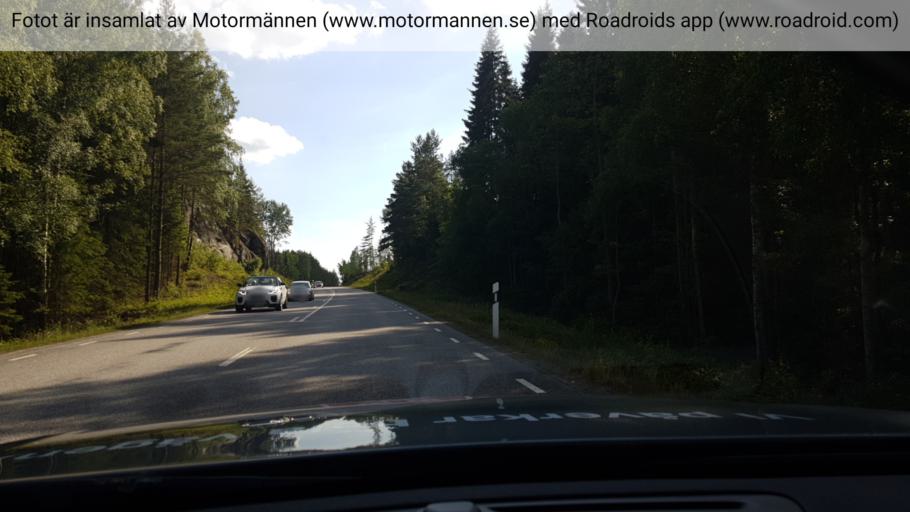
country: SE
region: Vaestra Goetaland
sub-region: Karlsborgs Kommun
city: Karlsborg
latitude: 58.6588
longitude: 14.5893
